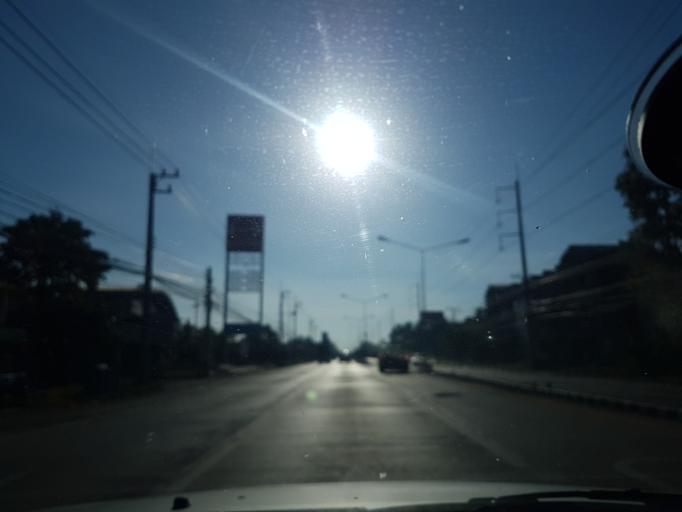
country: TH
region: Lop Buri
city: Lop Buri
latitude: 14.7694
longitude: 100.7057
